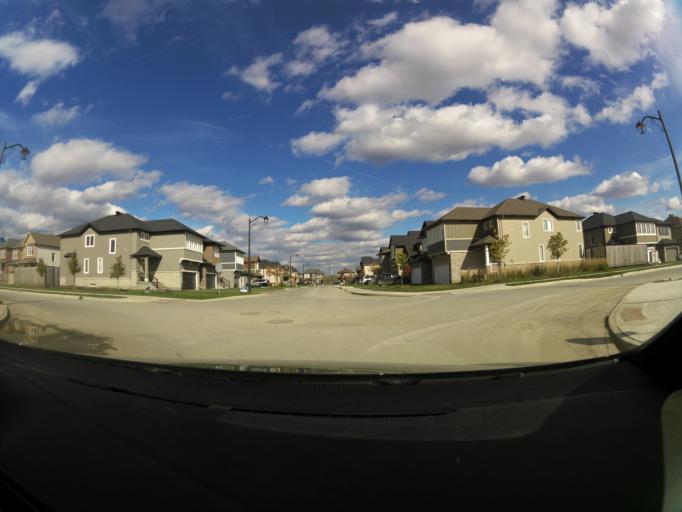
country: CA
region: Ontario
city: Bells Corners
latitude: 45.2770
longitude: -75.8819
